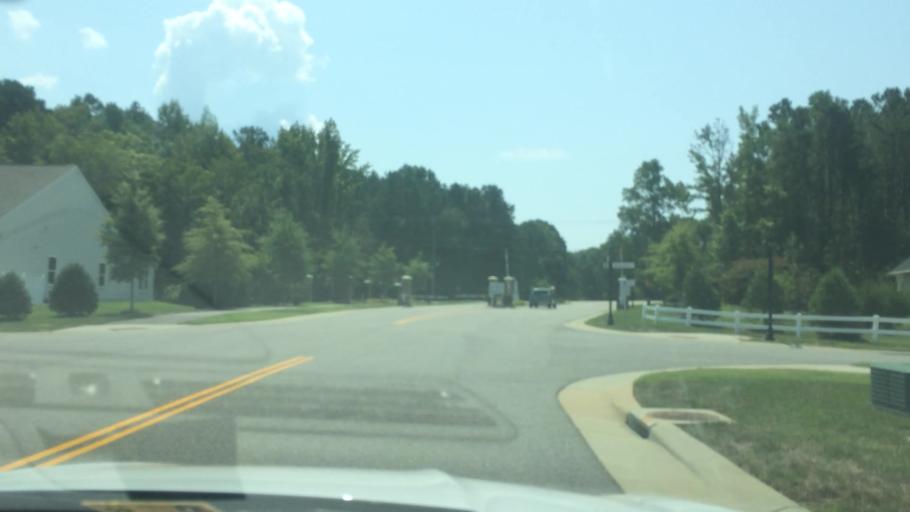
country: US
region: Virginia
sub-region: James City County
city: Williamsburg
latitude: 37.3361
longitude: -76.7758
